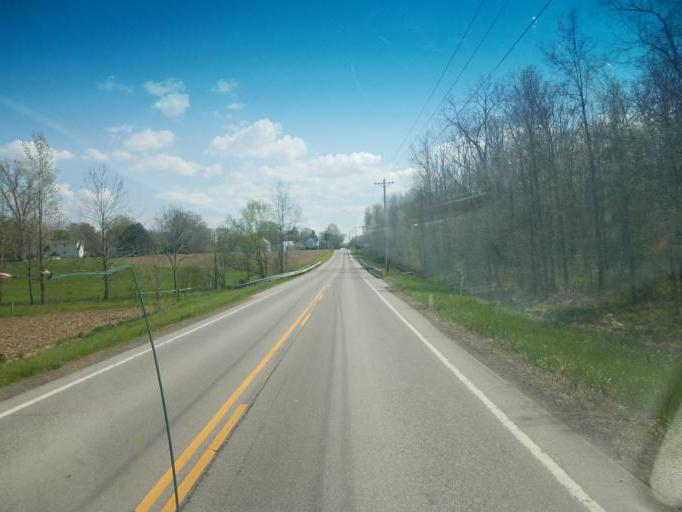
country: US
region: Ohio
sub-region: Wayne County
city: West Salem
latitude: 40.9205
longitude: -82.1090
